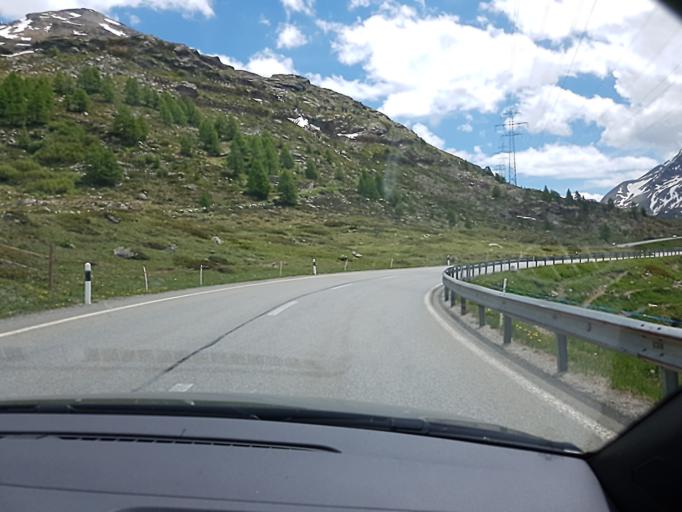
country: CH
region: Grisons
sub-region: Maloja District
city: Pontresina
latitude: 46.4328
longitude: 9.9976
